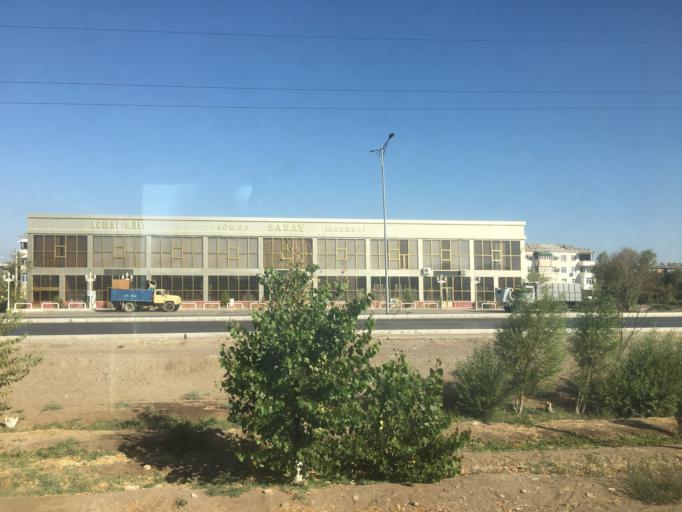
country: TM
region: Lebap
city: Turkmenabat
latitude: 39.0656
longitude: 63.5718
